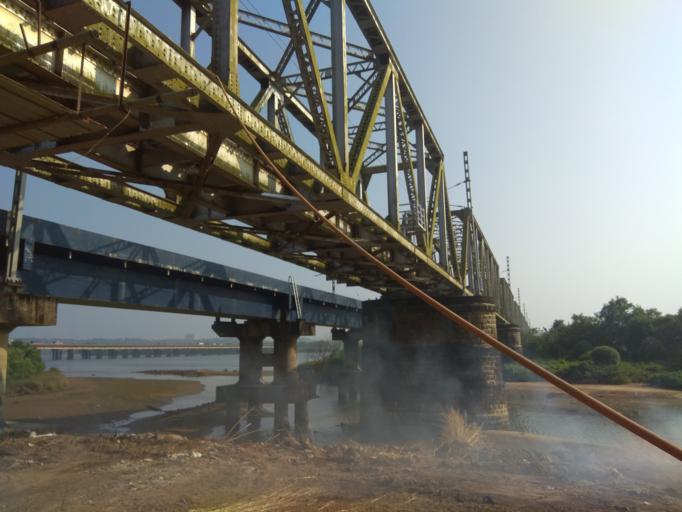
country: IN
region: Karnataka
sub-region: Dakshina Kannada
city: Ullal
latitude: 12.8431
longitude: 74.8562
